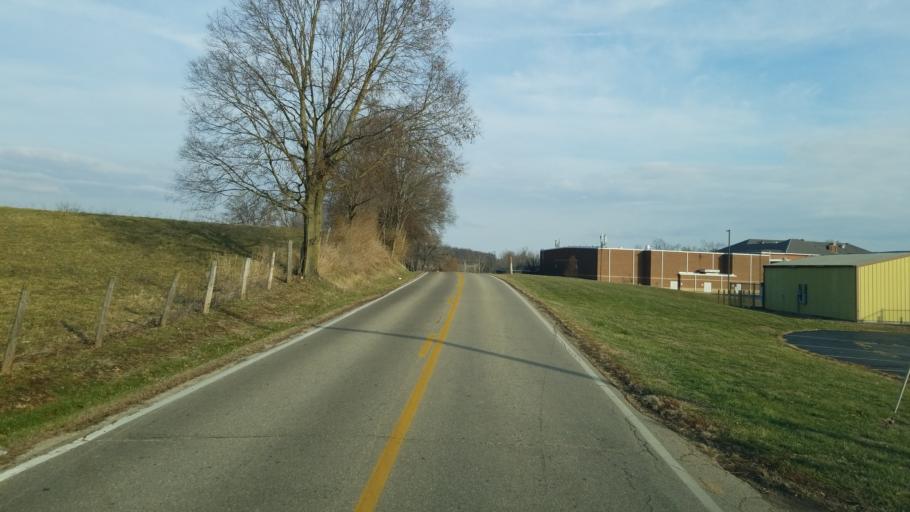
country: US
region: Ohio
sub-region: Ross County
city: Kingston
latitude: 39.4257
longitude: -82.9391
